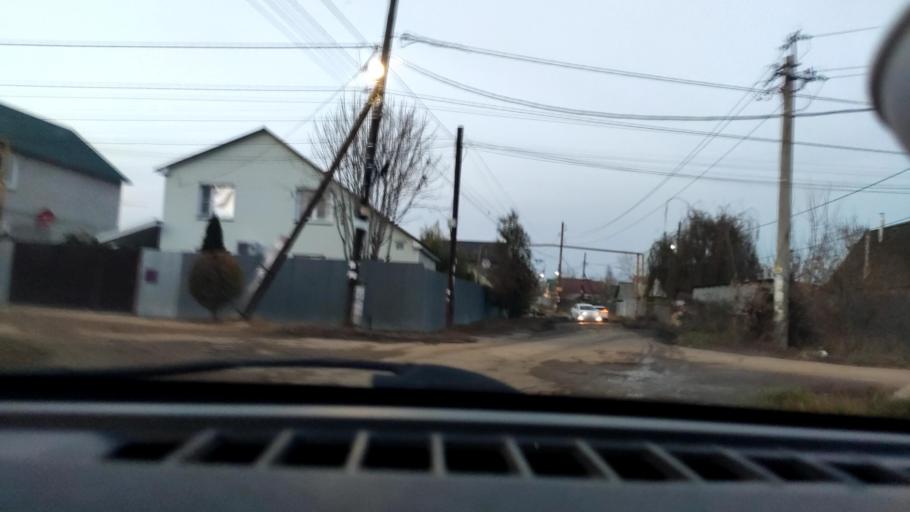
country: RU
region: Samara
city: Samara
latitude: 53.1389
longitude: 50.0961
